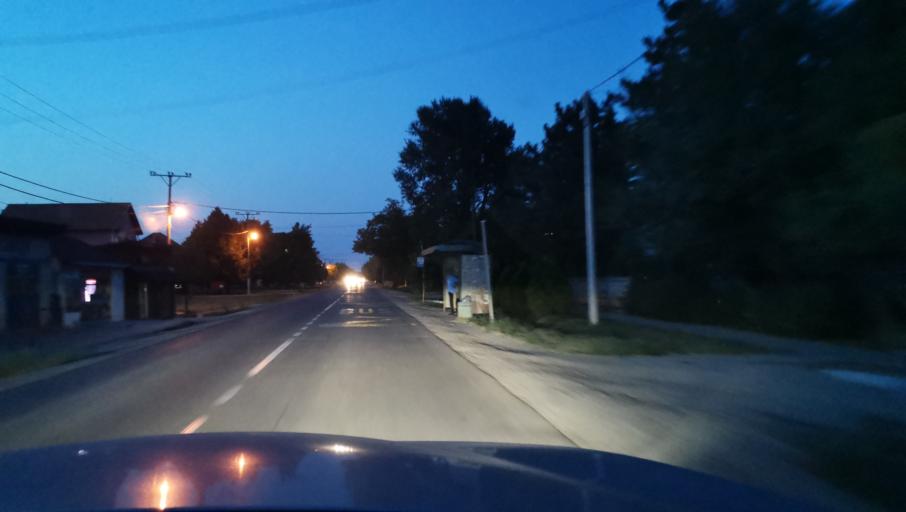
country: RS
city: Boljevci
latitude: 44.7454
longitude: 20.2538
